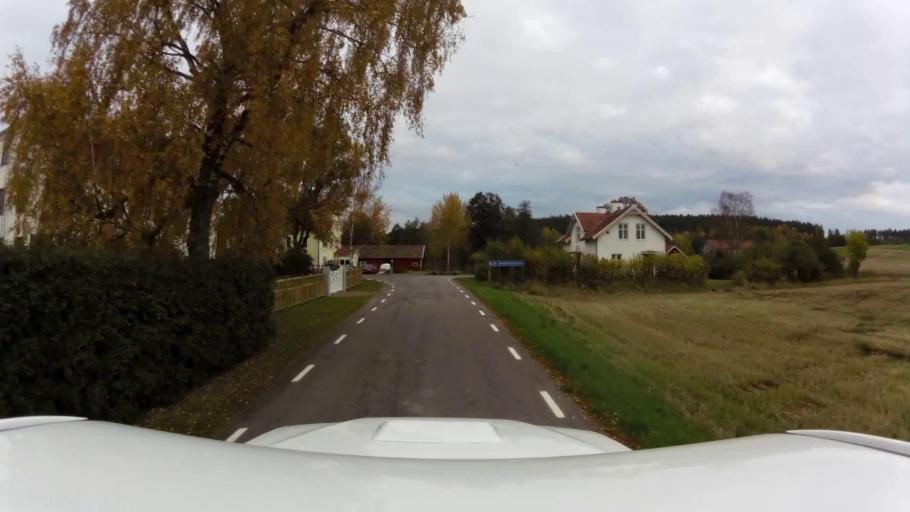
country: SE
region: OEstergoetland
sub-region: Linkopings Kommun
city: Ljungsbro
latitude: 58.5346
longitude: 15.4187
